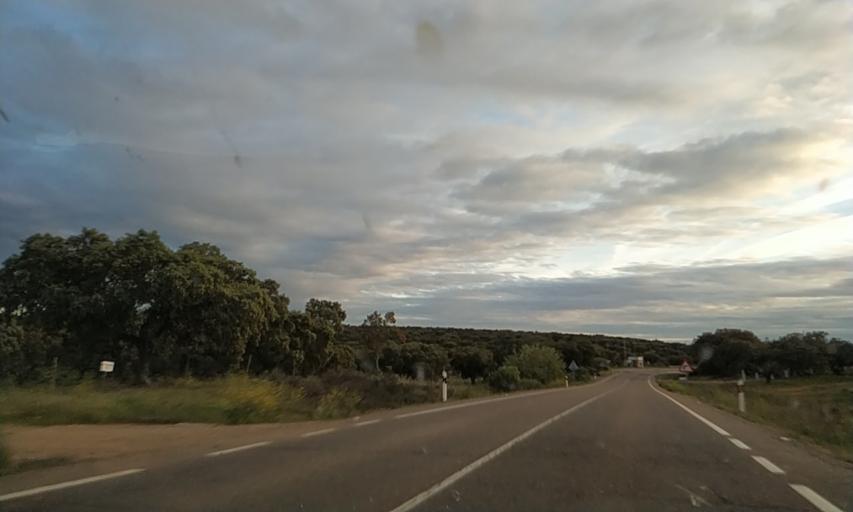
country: ES
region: Extremadura
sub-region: Provincia de Badajoz
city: La Roca de la Sierra
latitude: 39.1396
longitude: -6.6557
